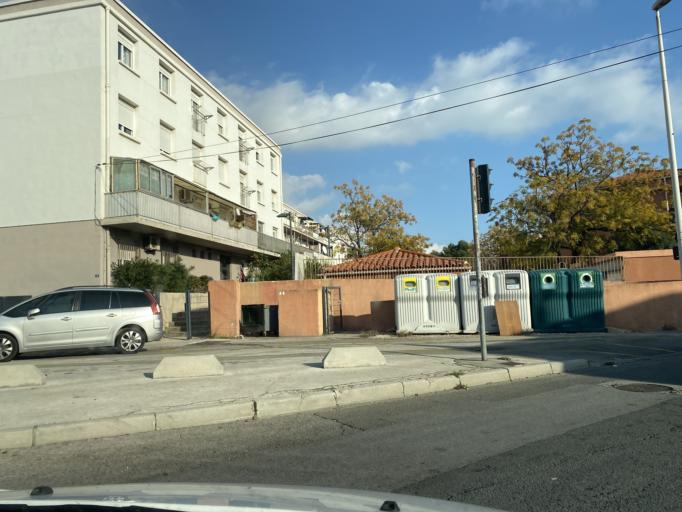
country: FR
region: Provence-Alpes-Cote d'Azur
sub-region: Departement du Var
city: Six-Fours-les-Plages
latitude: 43.1112
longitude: 5.8600
